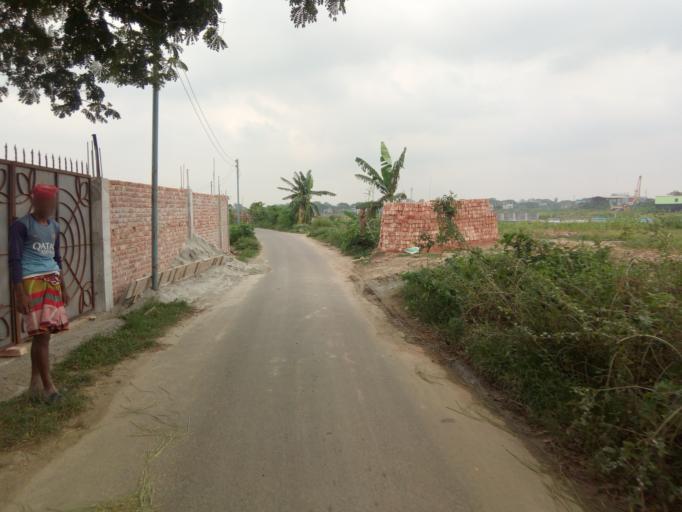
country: BD
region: Dhaka
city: Paltan
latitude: 23.7461
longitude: 90.4741
